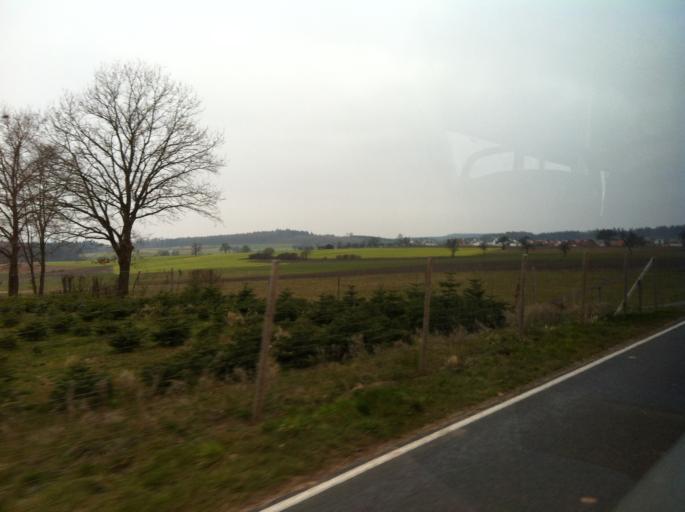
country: DE
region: Baden-Wuerttemberg
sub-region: Karlsruhe Region
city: Fahrenbach
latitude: 49.4210
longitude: 9.1591
